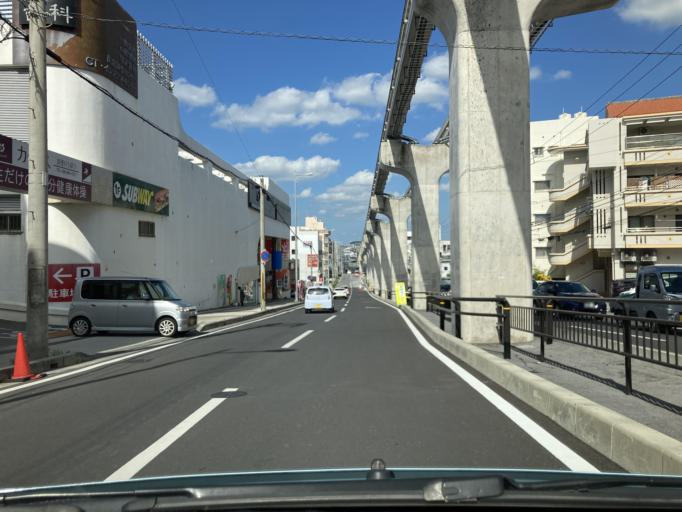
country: JP
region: Okinawa
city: Naha-shi
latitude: 26.2218
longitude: 127.7271
